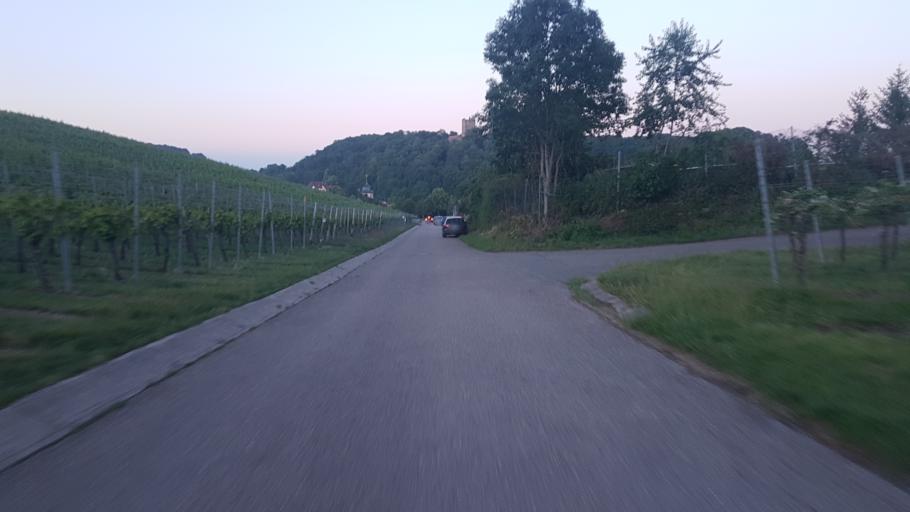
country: DE
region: Baden-Wuerttemberg
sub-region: Regierungsbezirk Stuttgart
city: Brackenheim
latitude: 49.1040
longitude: 9.0426
